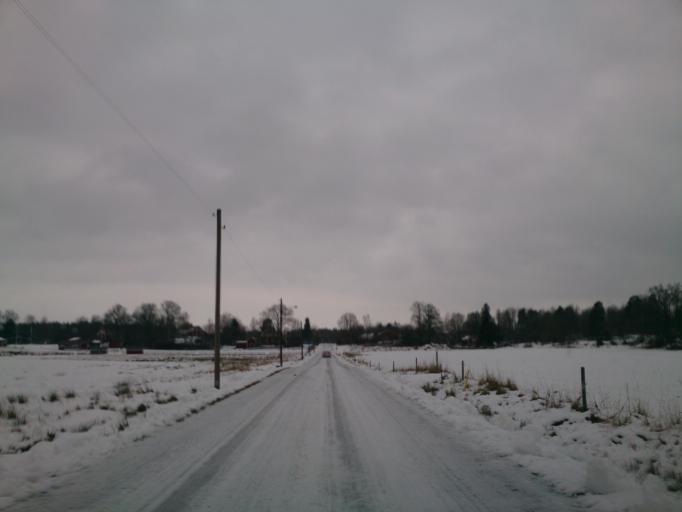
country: SE
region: OEstergoetland
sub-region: Atvidabergs Kommun
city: Atvidaberg
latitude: 58.3295
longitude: 16.0243
